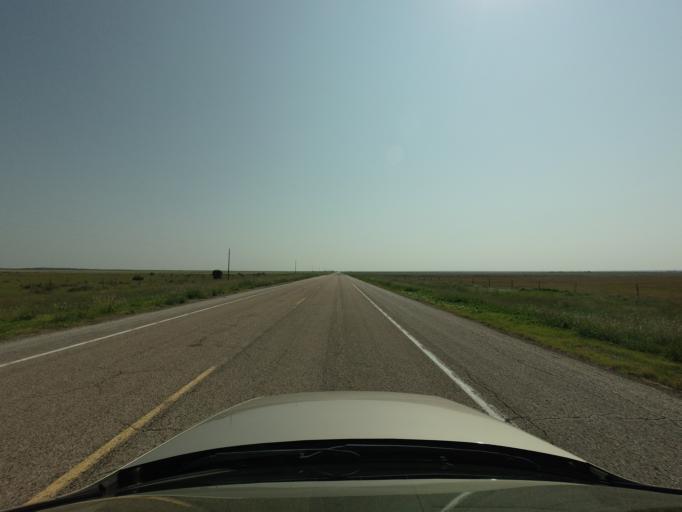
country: US
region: New Mexico
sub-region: Quay County
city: Tucumcari
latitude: 34.8234
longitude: -103.7351
